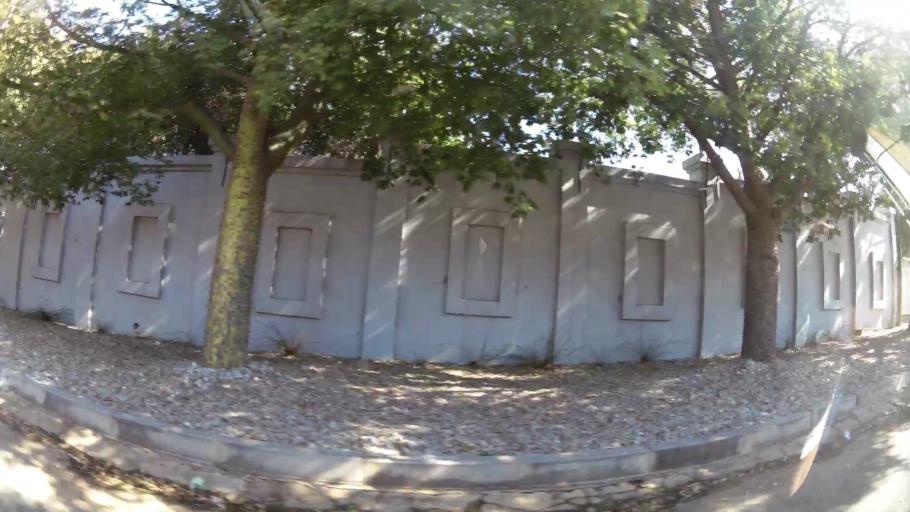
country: ZA
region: Gauteng
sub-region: City of Johannesburg Metropolitan Municipality
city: Modderfontein
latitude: -26.1538
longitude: 28.1230
